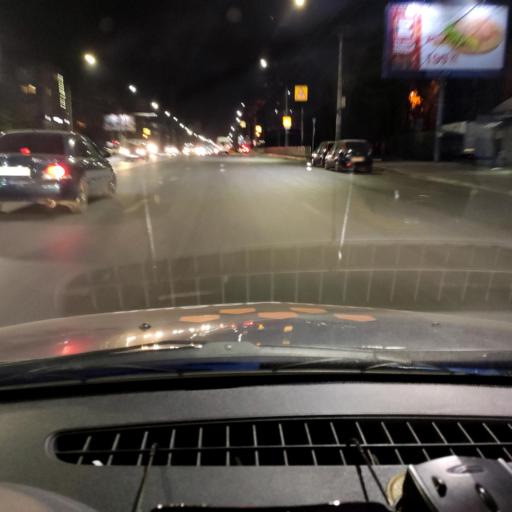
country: RU
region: Voronezj
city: Voronezh
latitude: 51.6707
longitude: 39.2516
